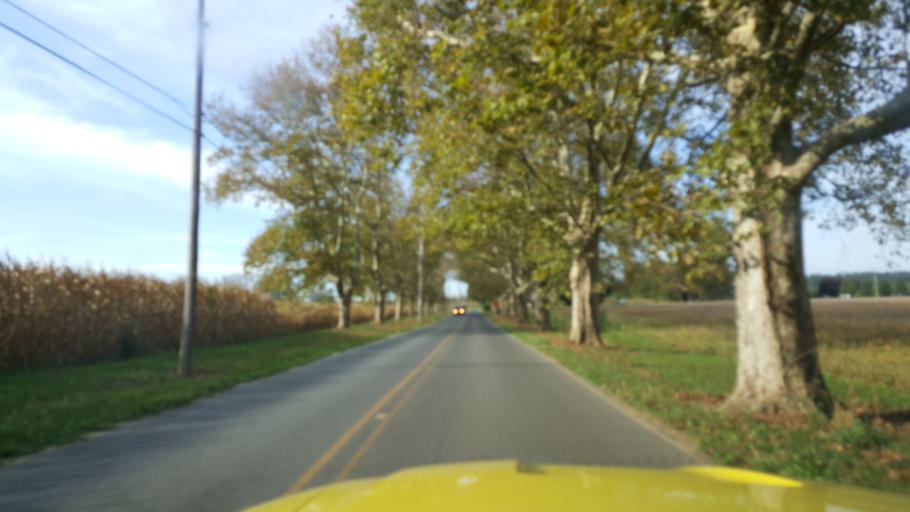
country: US
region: Pennsylvania
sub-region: Lebanon County
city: Annville
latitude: 40.3212
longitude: -76.5429
